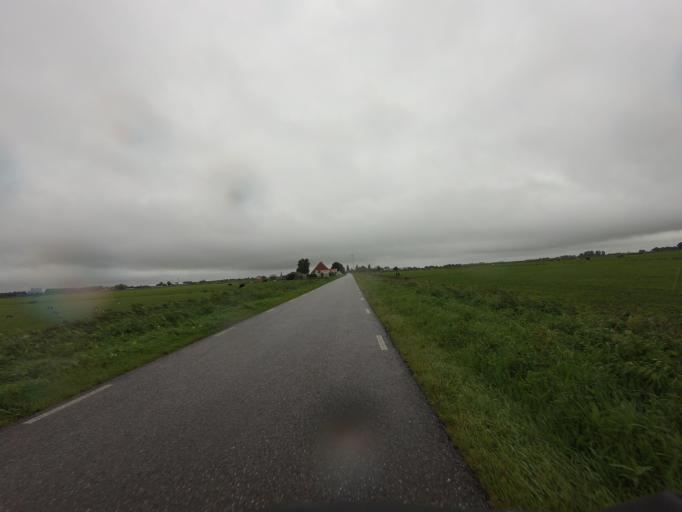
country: NL
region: Friesland
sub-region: Sudwest Fryslan
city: Workum
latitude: 52.9821
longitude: 5.4781
